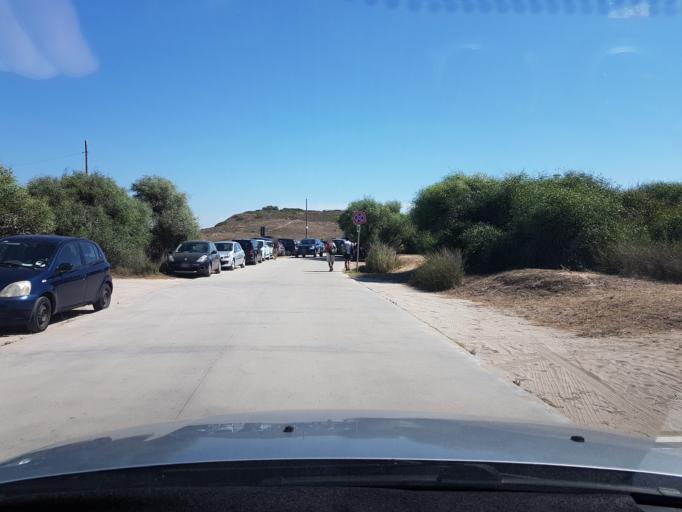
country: IT
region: Sardinia
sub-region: Provincia di Oristano
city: Cabras
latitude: 39.8808
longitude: 8.4393
